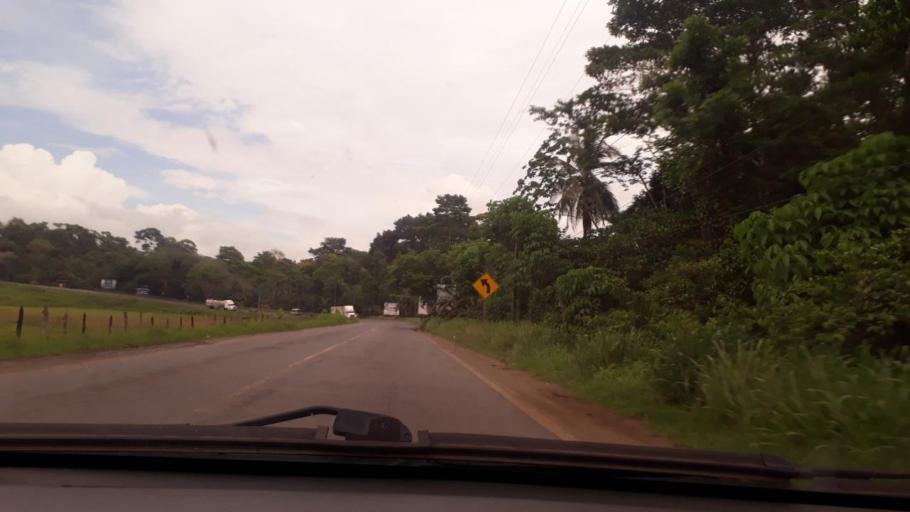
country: GT
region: Izabal
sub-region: Municipio de Puerto Barrios
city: Puerto Barrios
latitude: 15.6205
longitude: -88.5614
